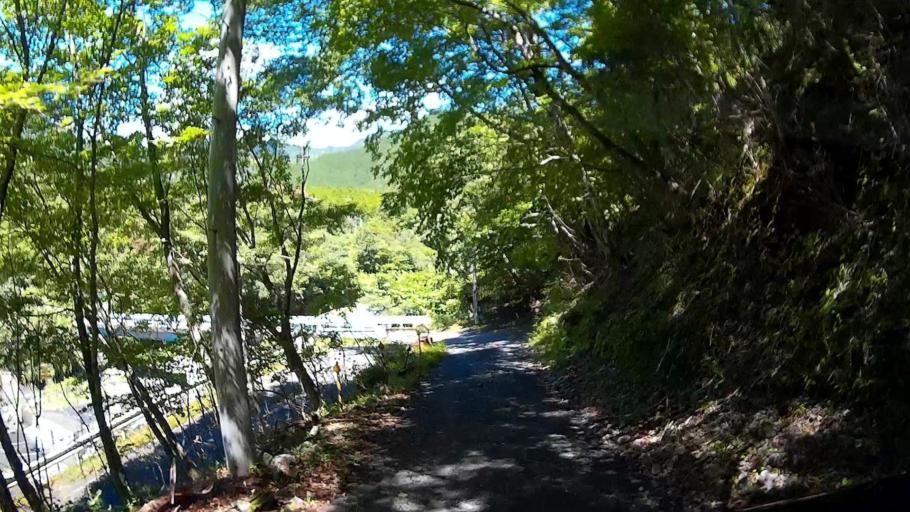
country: JP
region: Shizuoka
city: Fujinomiya
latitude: 35.2824
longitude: 138.3237
